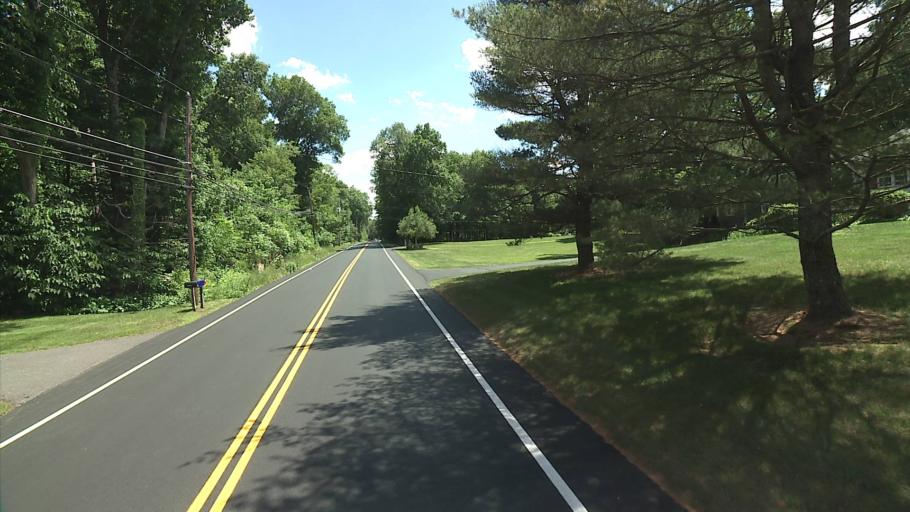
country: US
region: Connecticut
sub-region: Tolland County
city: Somers
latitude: 41.9991
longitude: -72.4327
